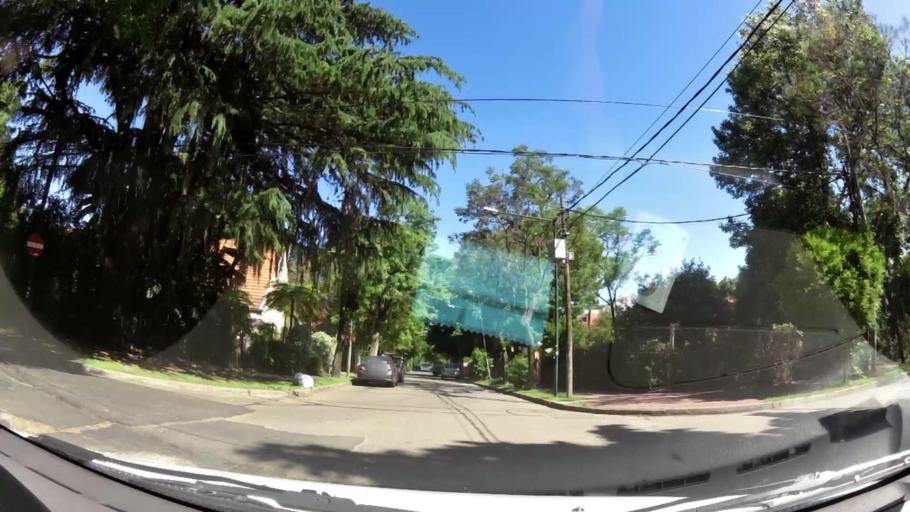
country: AR
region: Buenos Aires
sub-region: Partido de San Isidro
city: San Isidro
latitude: -34.4565
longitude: -58.5251
